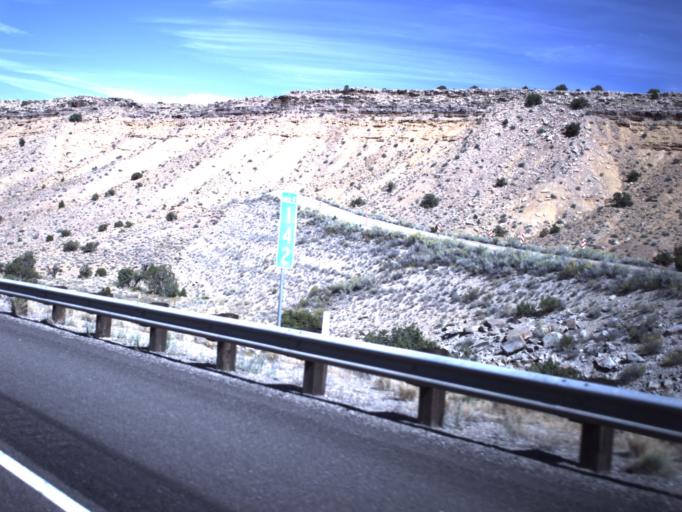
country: US
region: Utah
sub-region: Emery County
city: Castle Dale
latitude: 38.9322
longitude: -110.4890
